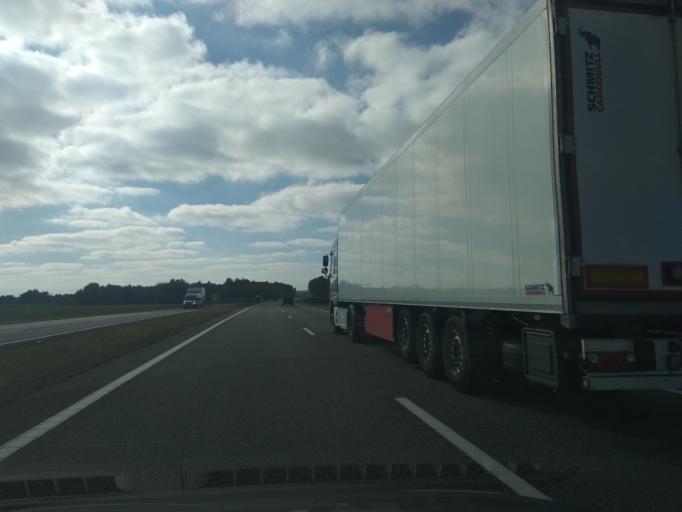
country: BY
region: Grodnenskaya
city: Mir
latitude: 53.4205
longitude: 26.5761
